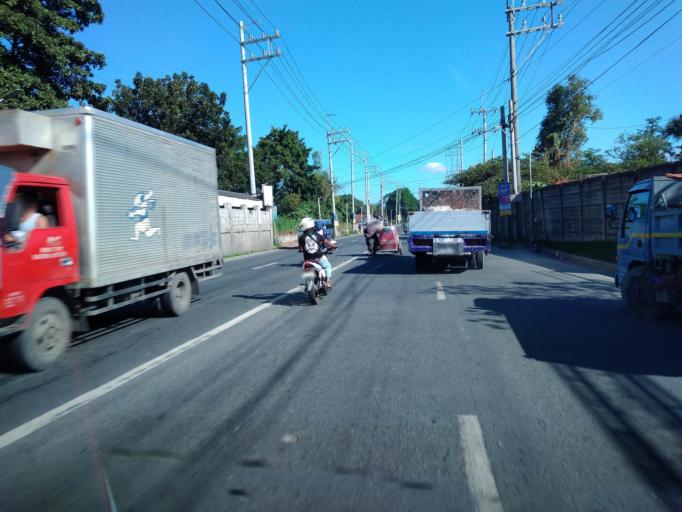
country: PH
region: Central Luzon
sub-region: Province of Bulacan
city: Santa Maria
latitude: 14.8148
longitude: 120.9488
